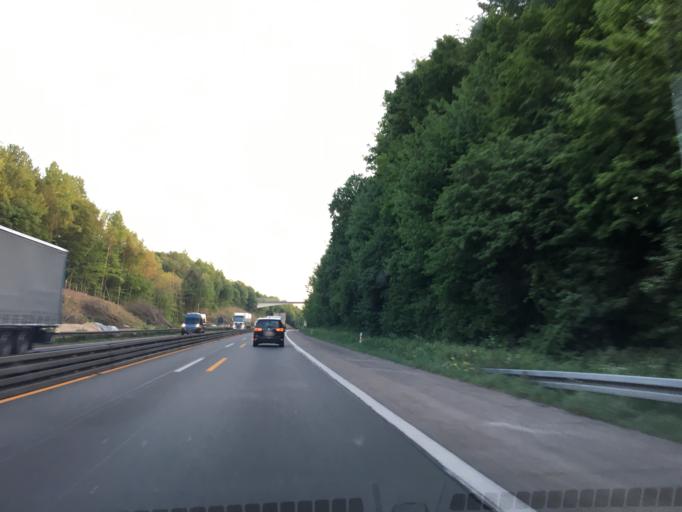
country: DE
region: North Rhine-Westphalia
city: Lengerich
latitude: 52.2210
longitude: 7.8704
